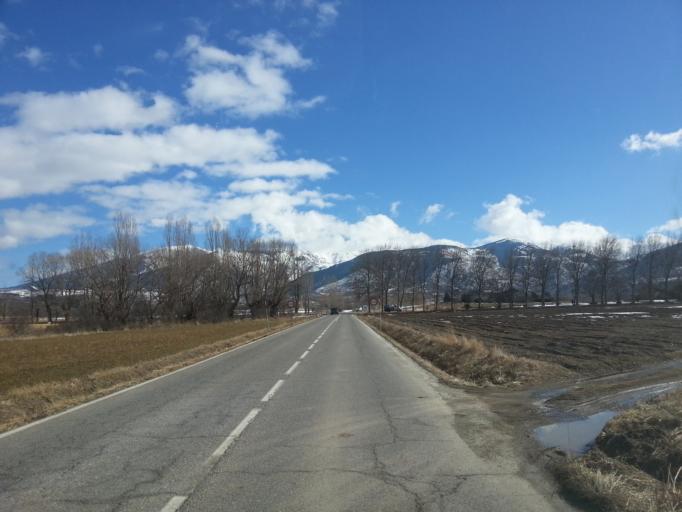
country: ES
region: Catalonia
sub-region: Provincia de Girona
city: Llivia
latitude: 42.4592
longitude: 1.9997
